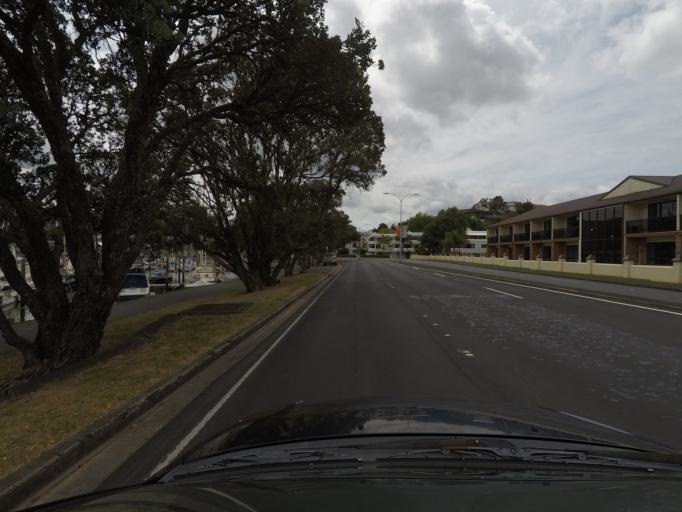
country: NZ
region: Northland
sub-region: Whangarei
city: Whangarei
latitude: -35.7240
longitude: 174.3274
